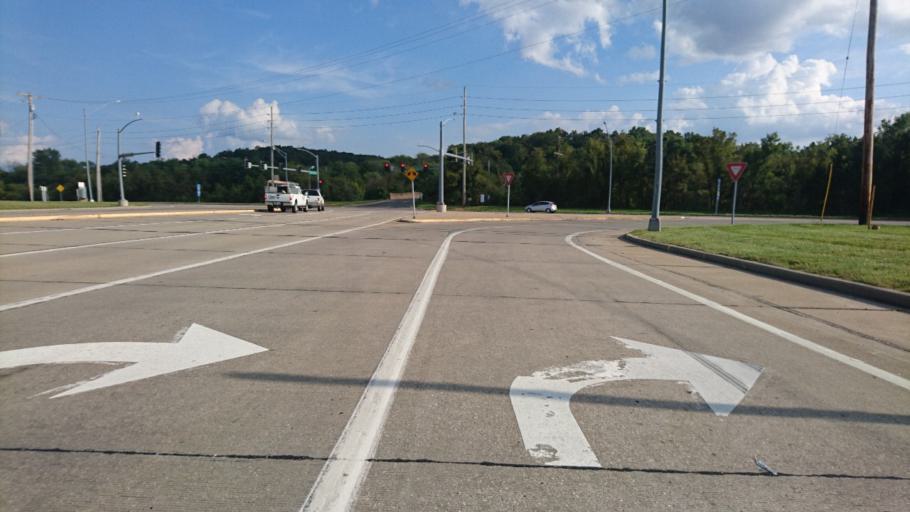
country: US
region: Missouri
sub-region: Saint Louis County
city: Eureka
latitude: 38.5050
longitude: -90.6771
